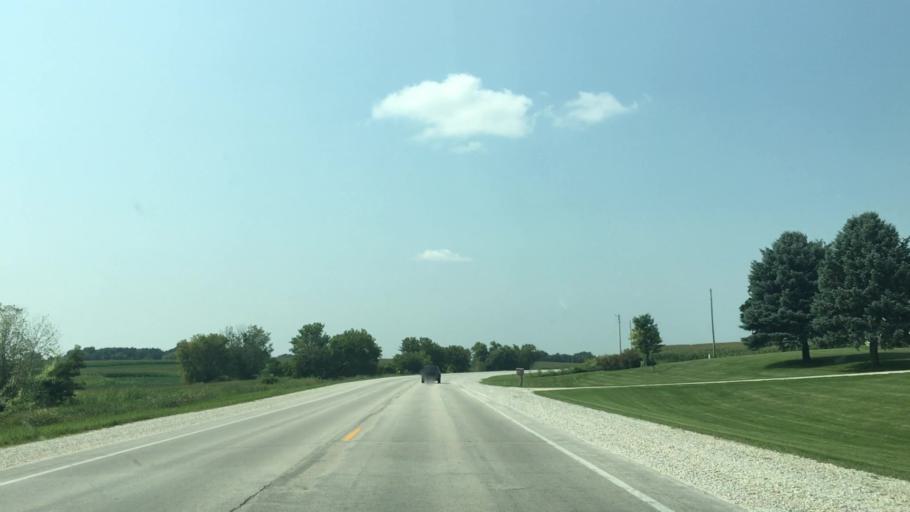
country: US
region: Iowa
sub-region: Winneshiek County
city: Decorah
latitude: 43.4043
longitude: -91.8512
